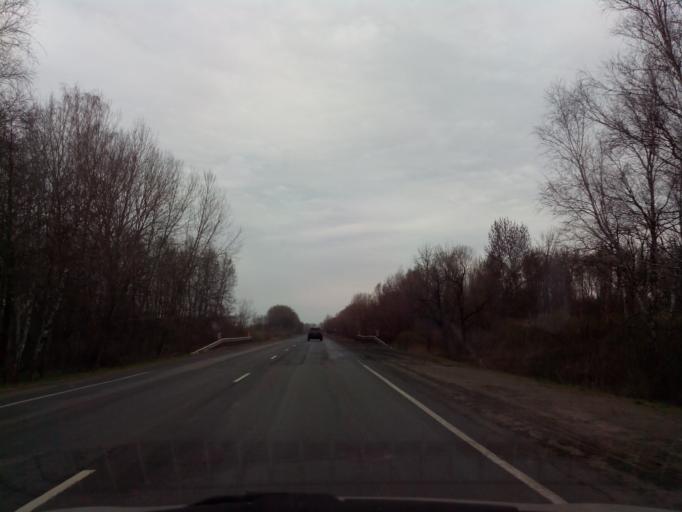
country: RU
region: Tambov
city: Zavoronezhskoye
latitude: 52.9392
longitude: 40.6005
